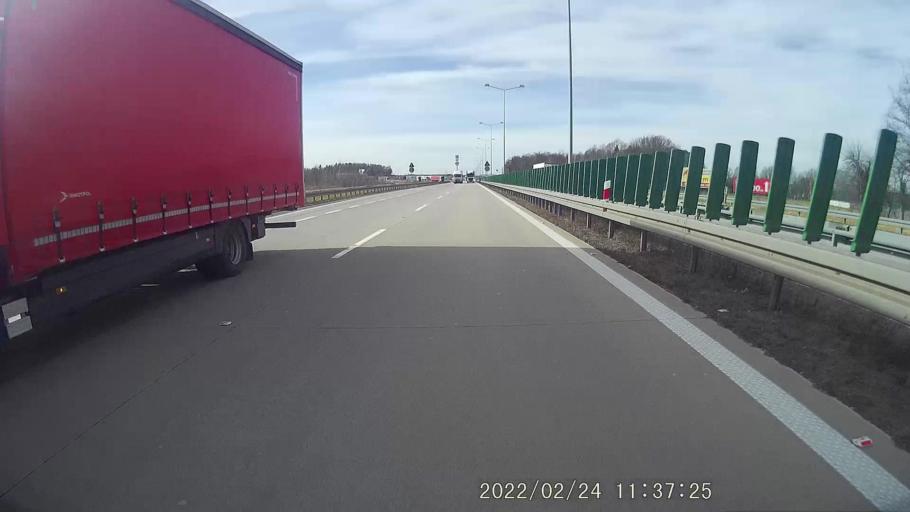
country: PL
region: Lower Silesian Voivodeship
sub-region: Powiat polkowicki
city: Przemkow
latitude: 51.5226
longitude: 15.8265
